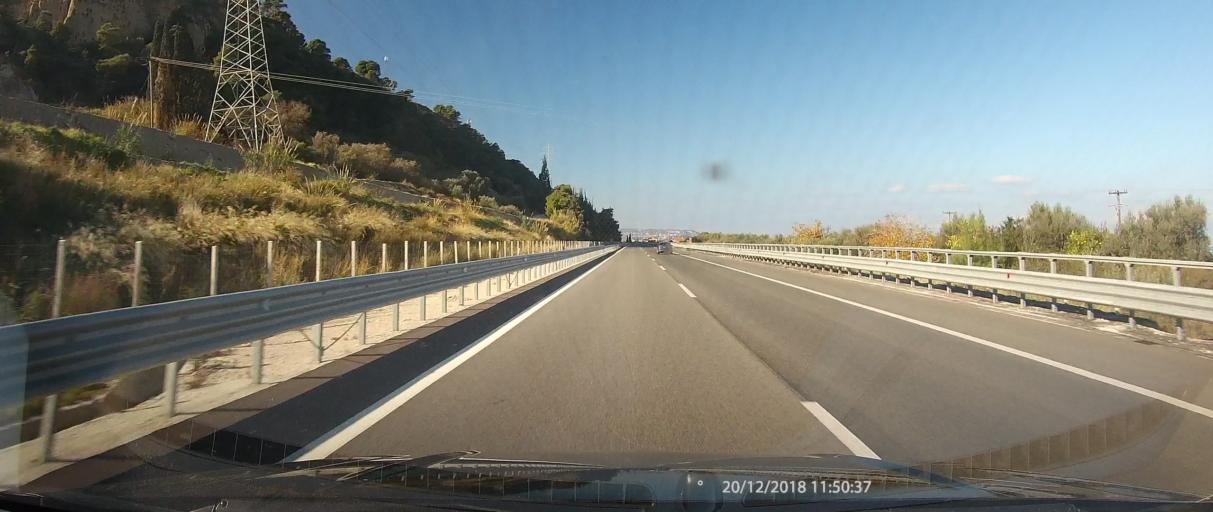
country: GR
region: West Greece
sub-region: Nomos Achaias
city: Aiyira
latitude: 38.1324
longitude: 22.4378
